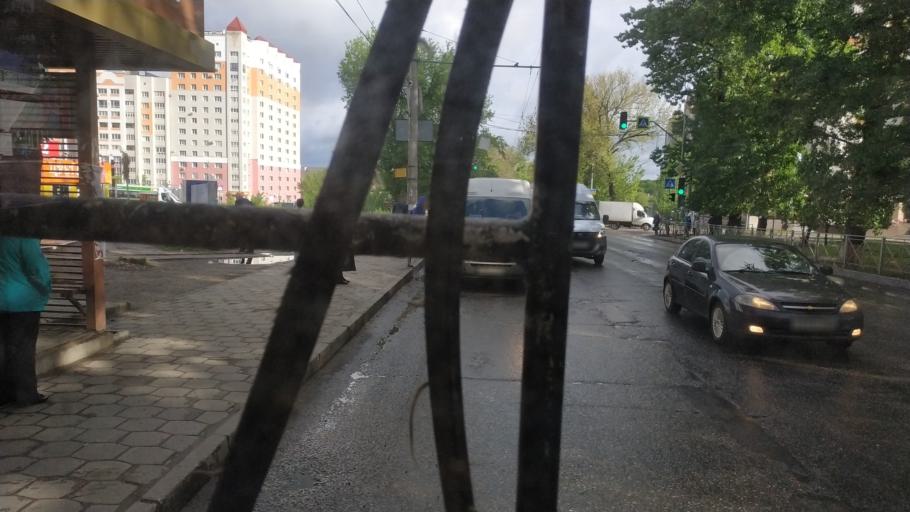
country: RU
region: Brjansk
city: Putevka
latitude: 53.2645
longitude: 34.3234
